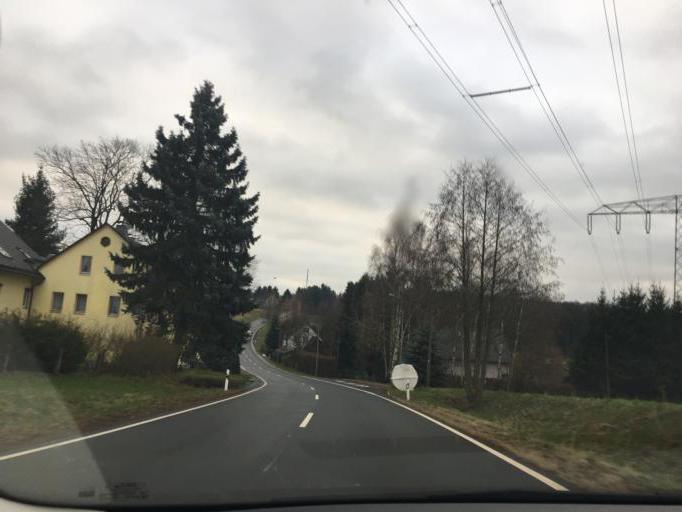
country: DE
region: Saxony
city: Hohenstein-Ernstthal
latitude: 50.8176
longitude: 12.7039
